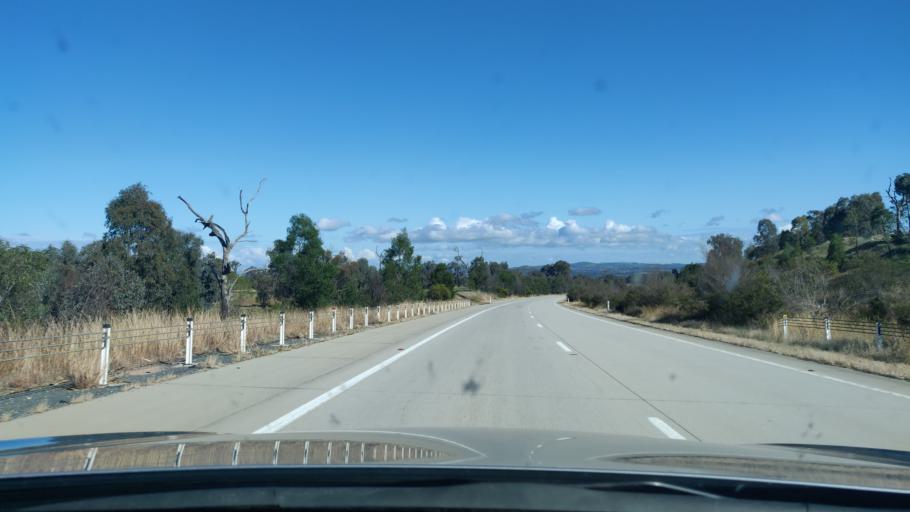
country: AU
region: New South Wales
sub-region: Albury Municipality
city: Lavington
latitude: -35.9245
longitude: 147.0906
